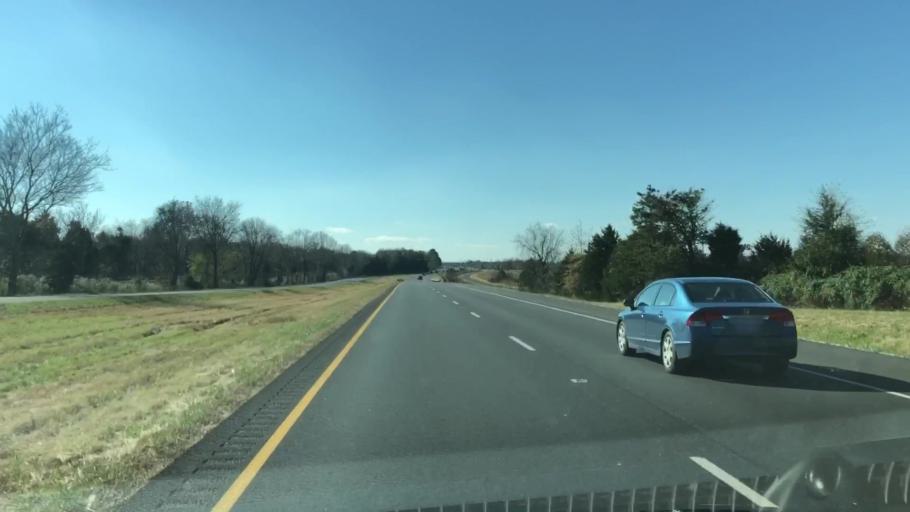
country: US
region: Virginia
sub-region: Fauquier County
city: Bealeton
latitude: 38.5165
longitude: -77.8421
